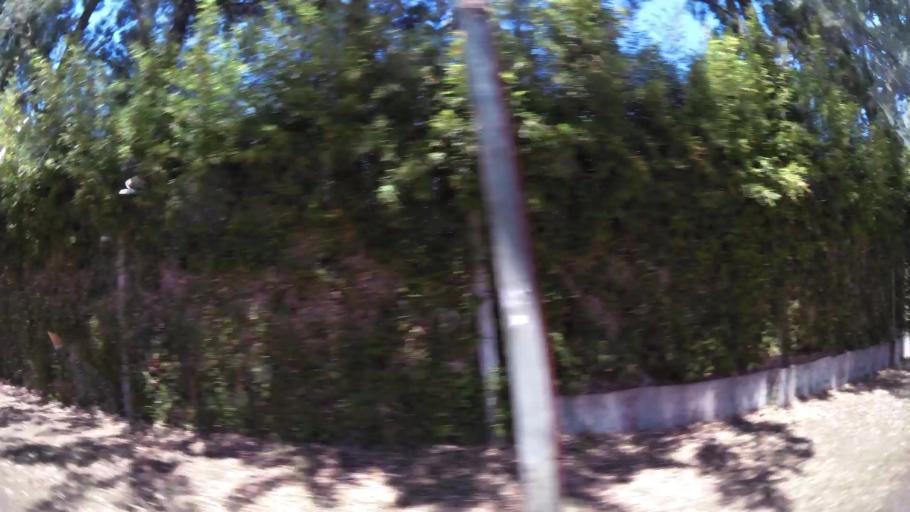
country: AR
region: Buenos Aires
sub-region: Partido de Tigre
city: Tigre
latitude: -34.4426
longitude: -58.5404
